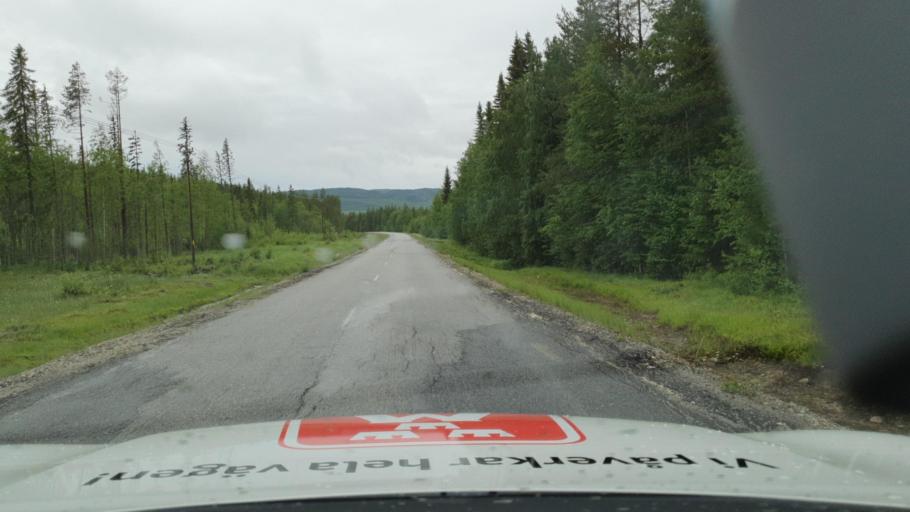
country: SE
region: Vaesterbotten
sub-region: Asele Kommun
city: Asele
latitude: 64.0019
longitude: 17.1845
